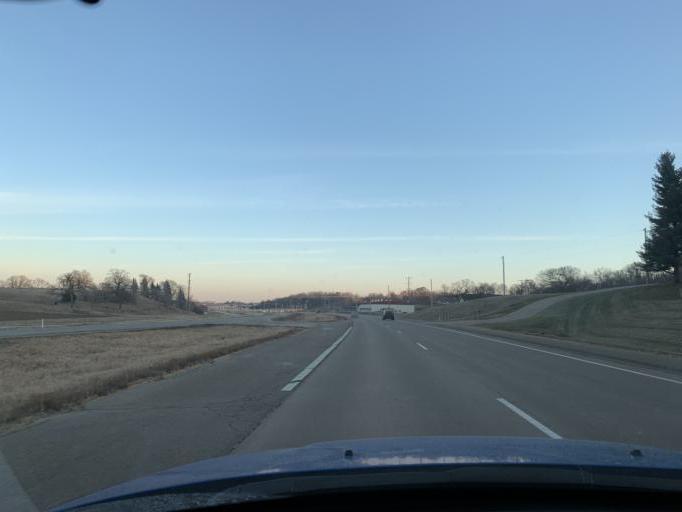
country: US
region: Wisconsin
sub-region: Dane County
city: Cross Plains
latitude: 43.1945
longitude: -89.5788
